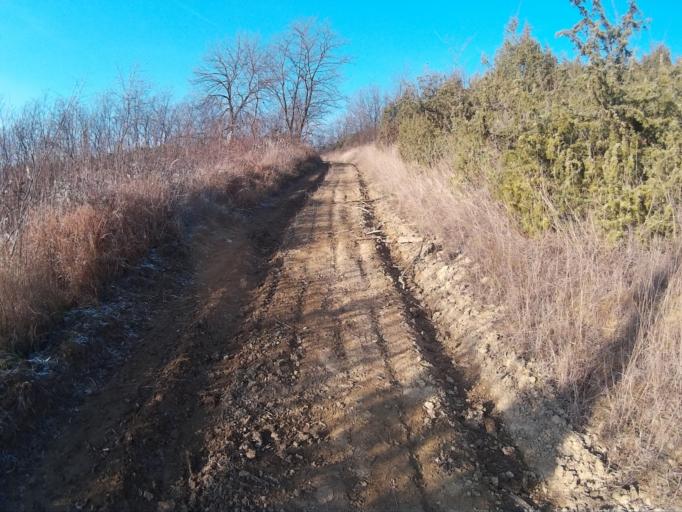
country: HU
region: Nograd
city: Bercel
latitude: 47.9612
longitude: 19.4393
